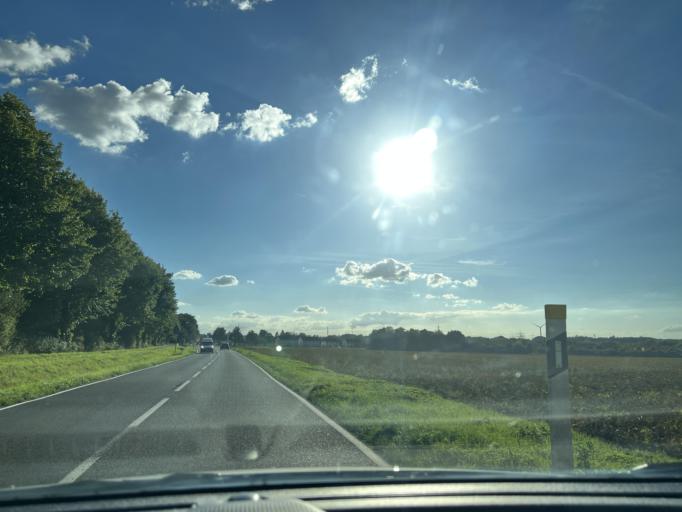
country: DE
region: North Rhine-Westphalia
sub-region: Regierungsbezirk Dusseldorf
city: Rommerskirchen
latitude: 50.9804
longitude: 6.6897
